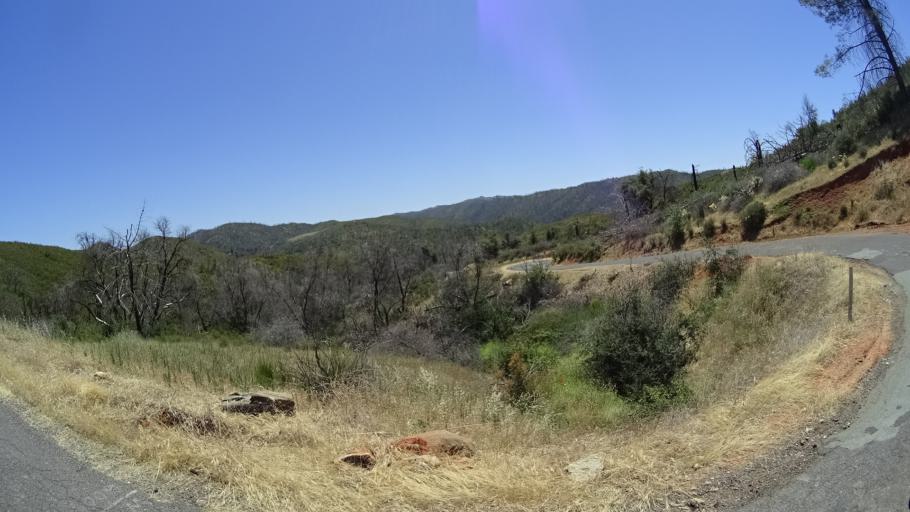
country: US
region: California
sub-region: Calaveras County
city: Mountain Ranch
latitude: 38.2893
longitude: -120.6229
